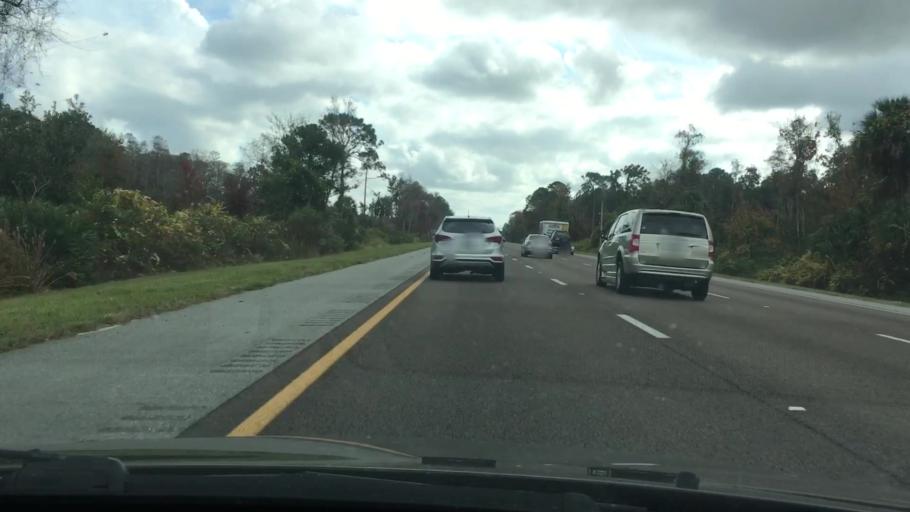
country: US
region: Florida
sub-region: Volusia County
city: Glencoe
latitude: 28.9745
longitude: -80.9632
